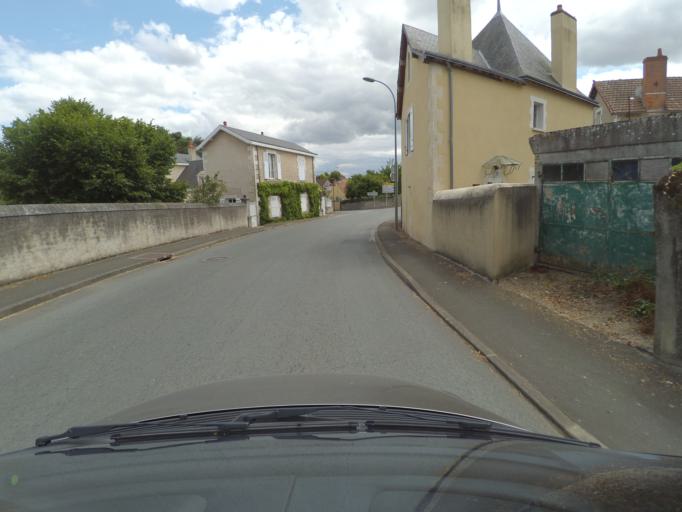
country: FR
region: Centre
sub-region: Departement de l'Indre
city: Belabre
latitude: 46.4680
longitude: 1.0402
